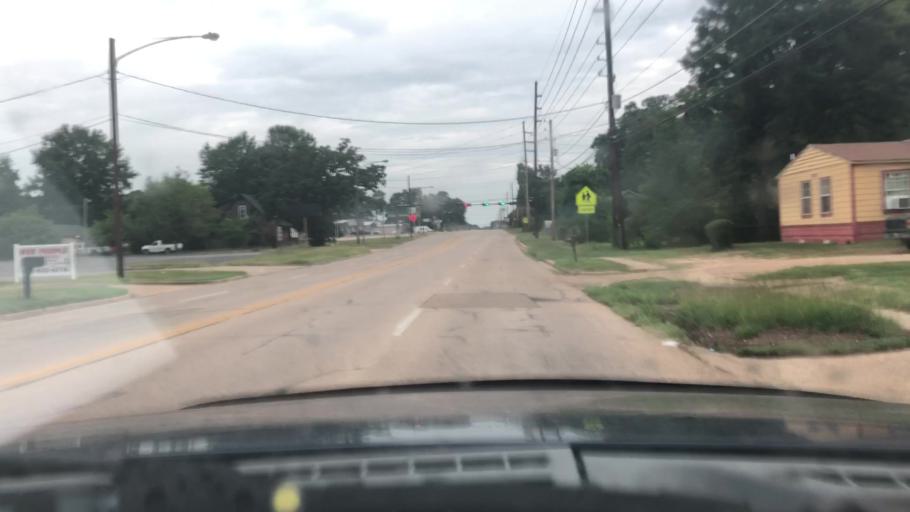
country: US
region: Texas
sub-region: Bowie County
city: Wake Village
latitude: 33.4296
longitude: -94.0803
